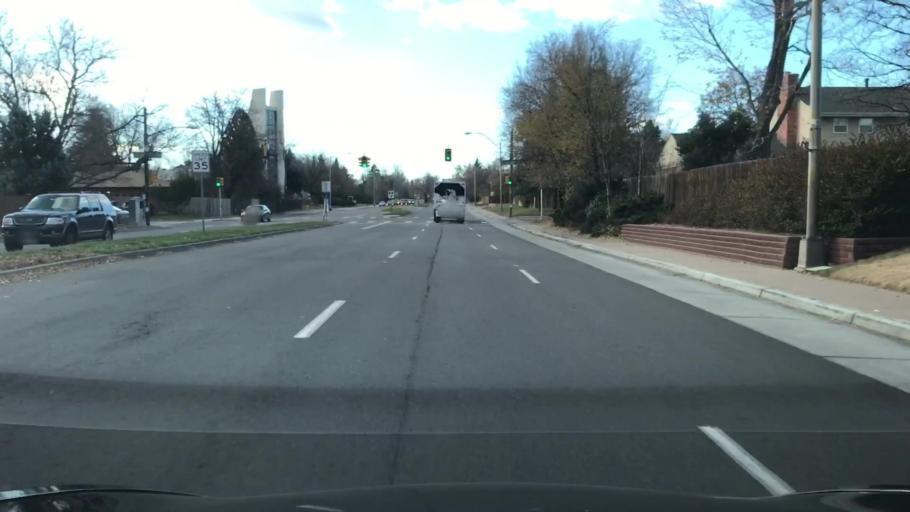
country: US
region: Colorado
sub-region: Arapahoe County
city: Glendale
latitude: 39.6634
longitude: -104.9130
